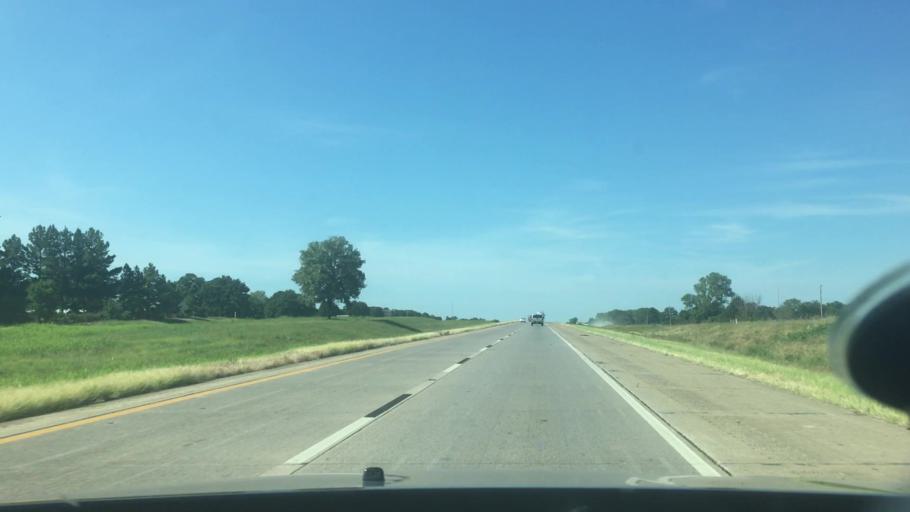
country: US
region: Oklahoma
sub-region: Atoka County
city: Atoka
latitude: 34.2085
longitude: -96.2348
